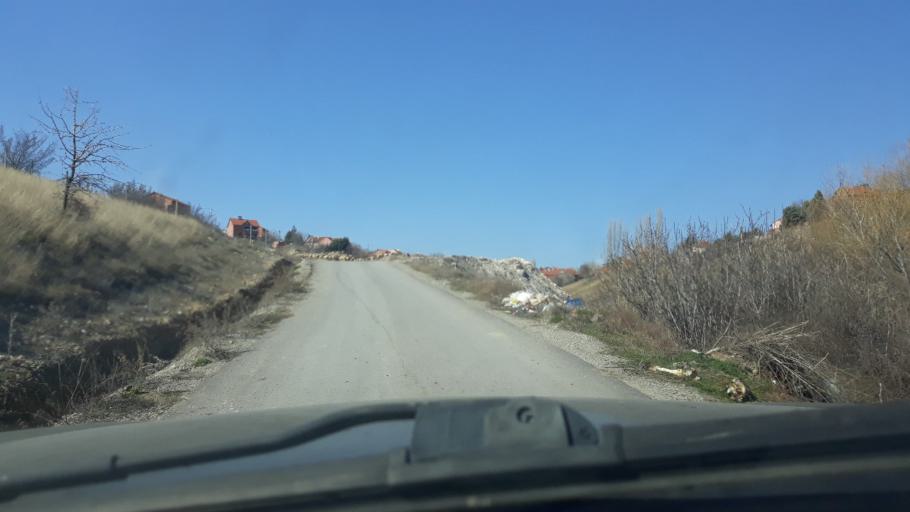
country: MK
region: Veles
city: Gorno Orizari
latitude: 41.6796
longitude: 21.7373
